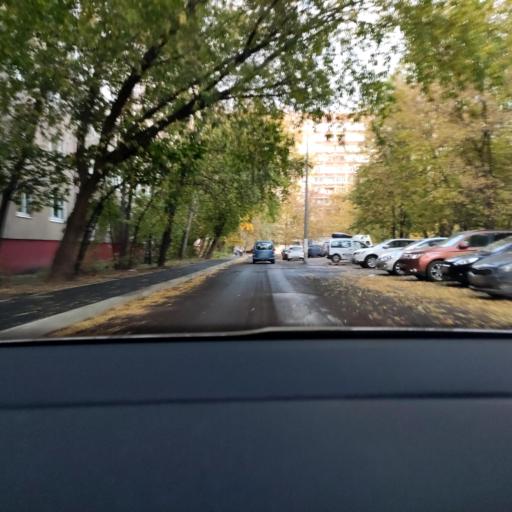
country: RU
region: Moscow
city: Otradnoye
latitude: 55.8666
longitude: 37.5917
